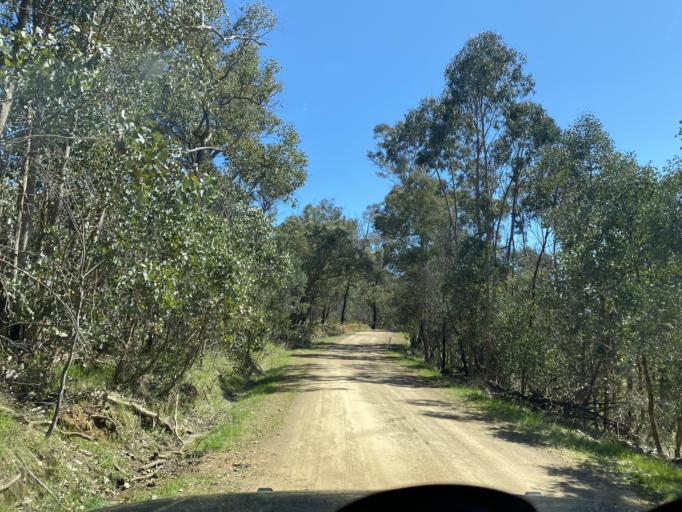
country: AU
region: Victoria
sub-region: Benalla
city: Benalla
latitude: -36.7075
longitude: 146.1783
